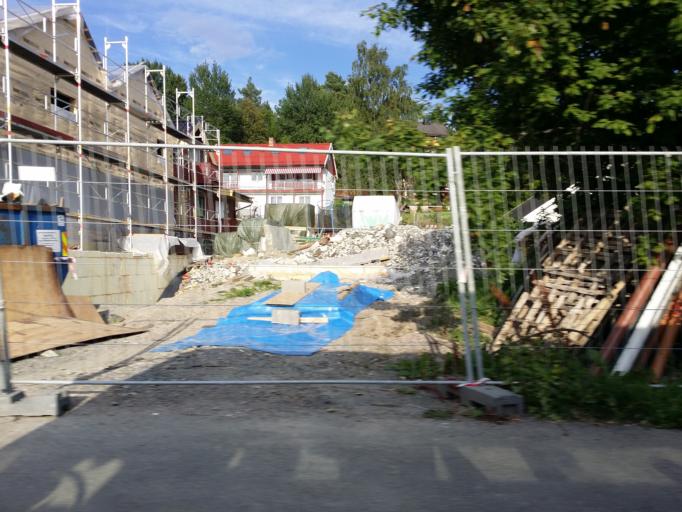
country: NO
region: Oslo
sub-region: Oslo
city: Oslo
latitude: 59.9072
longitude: 10.8511
